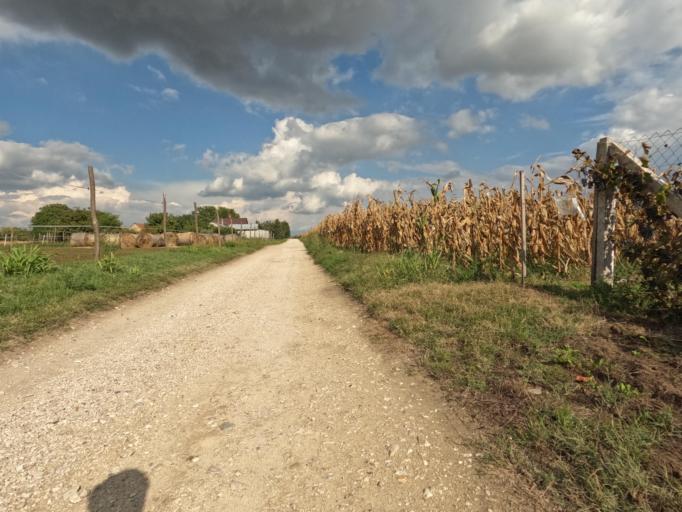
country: HU
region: Tolna
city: Tengelic
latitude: 46.5238
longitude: 18.7156
